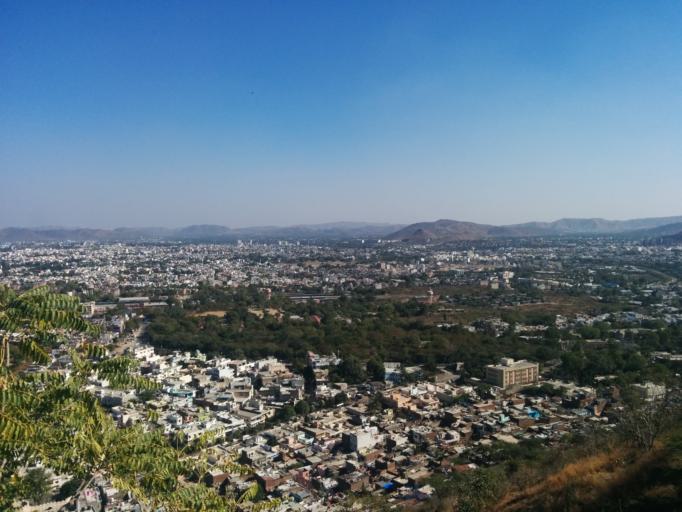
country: IN
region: Rajasthan
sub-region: Udaipur
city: Udaipur
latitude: 24.5669
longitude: 73.6890
